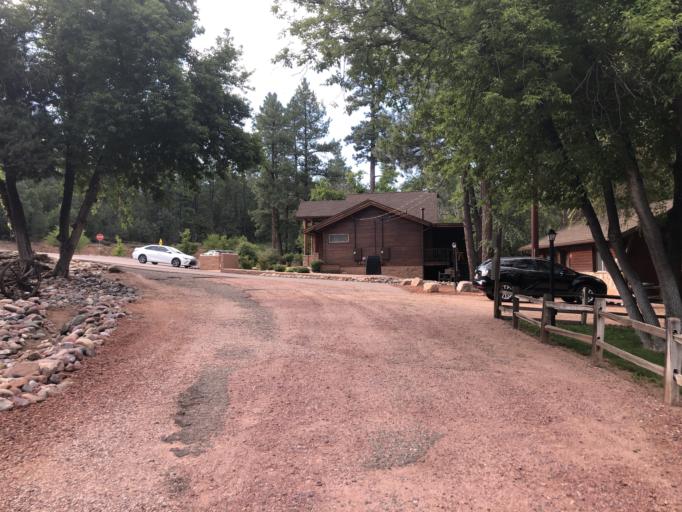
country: US
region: Arizona
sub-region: Gila County
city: Star Valley
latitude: 34.3256
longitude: -111.0936
